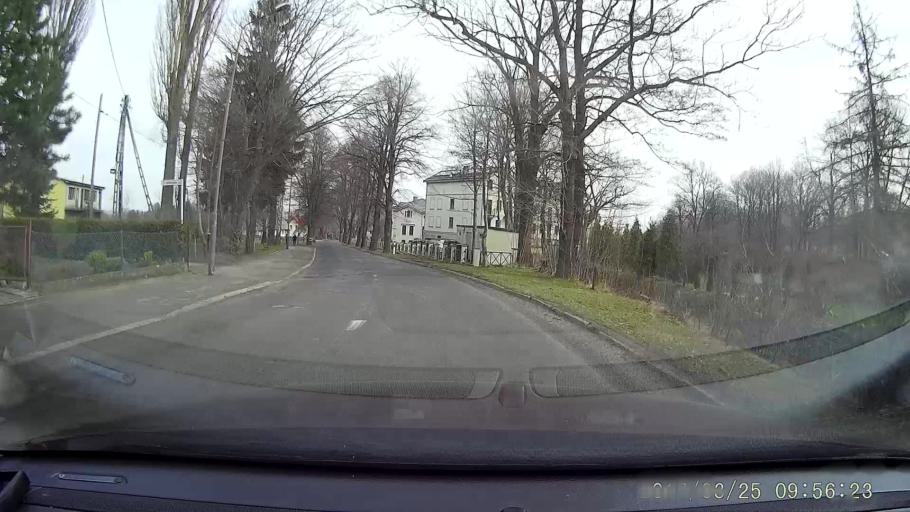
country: PL
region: Lower Silesian Voivodeship
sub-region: Powiat lubanski
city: Swieradow-Zdroj
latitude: 50.9248
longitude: 15.3061
